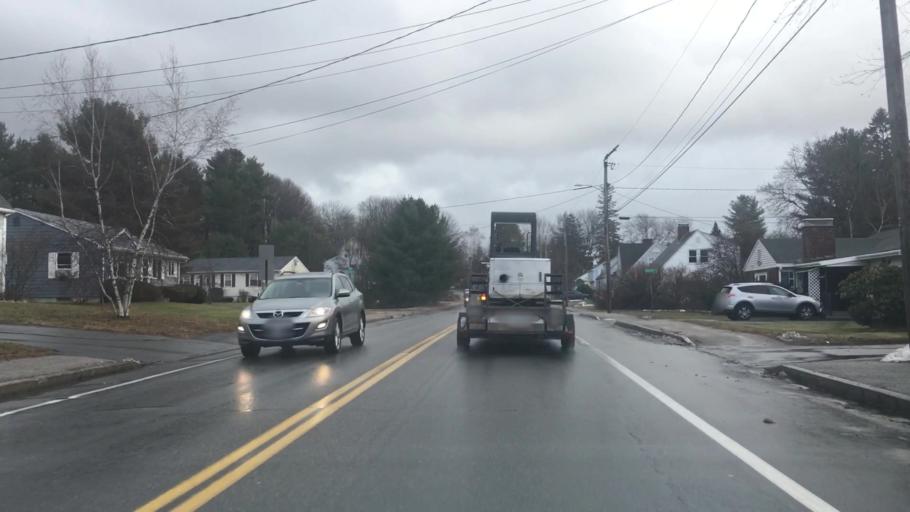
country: US
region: Maine
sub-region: Cumberland County
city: South Portland Gardens
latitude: 43.6635
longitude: -70.3050
